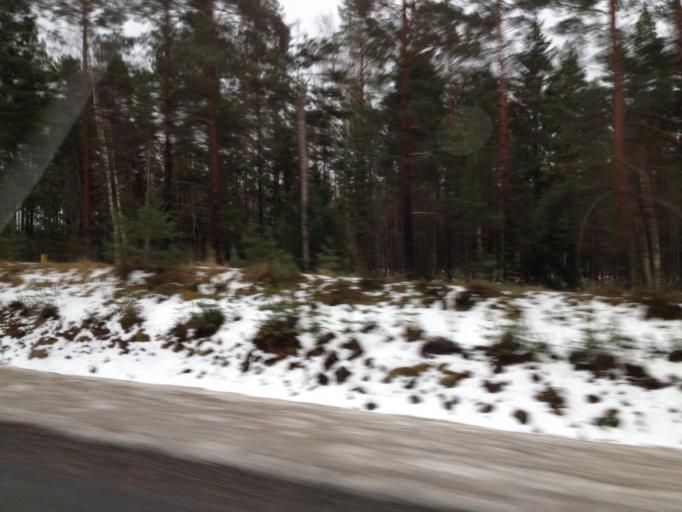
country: FI
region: Uusimaa
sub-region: Raaseporin
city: Hanko
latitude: 59.8610
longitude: 23.0464
